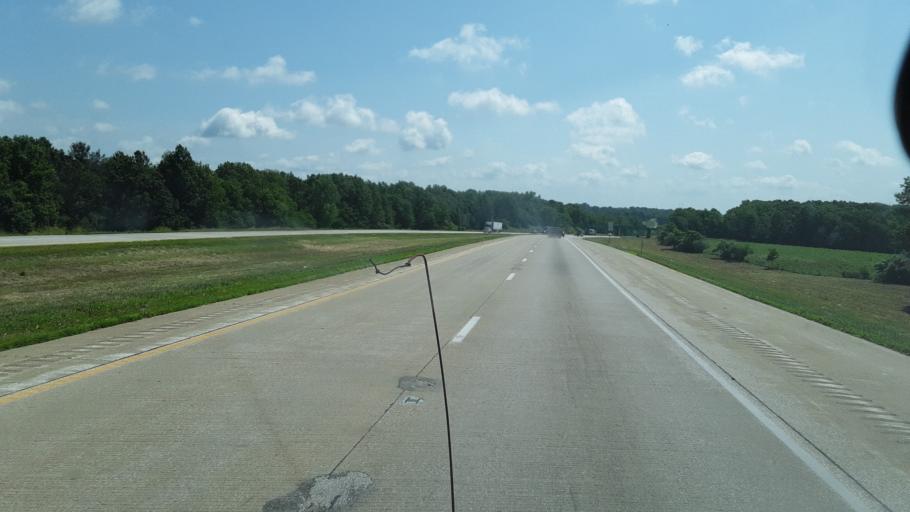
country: US
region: Illinois
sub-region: Clark County
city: Marshall
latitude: 39.4226
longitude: -87.6840
